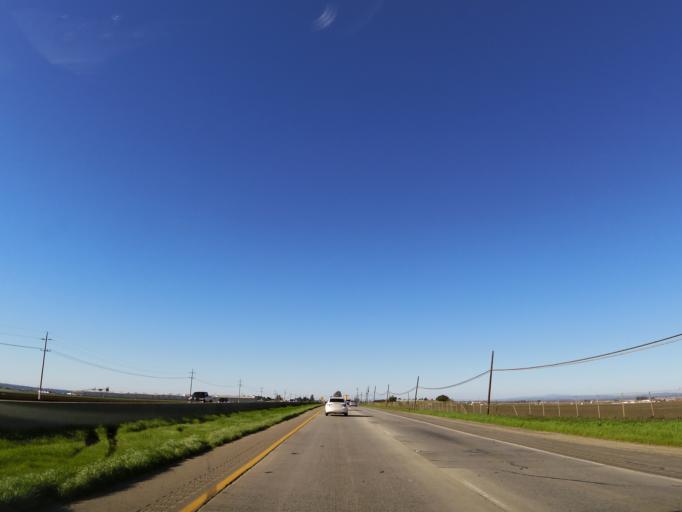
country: US
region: California
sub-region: Monterey County
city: Chualar
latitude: 36.6197
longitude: -121.5764
